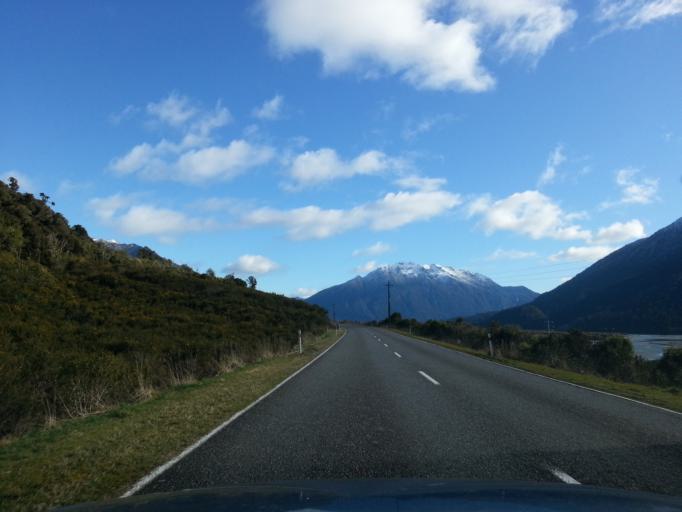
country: NZ
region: West Coast
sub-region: Grey District
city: Greymouth
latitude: -42.7367
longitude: 171.4343
